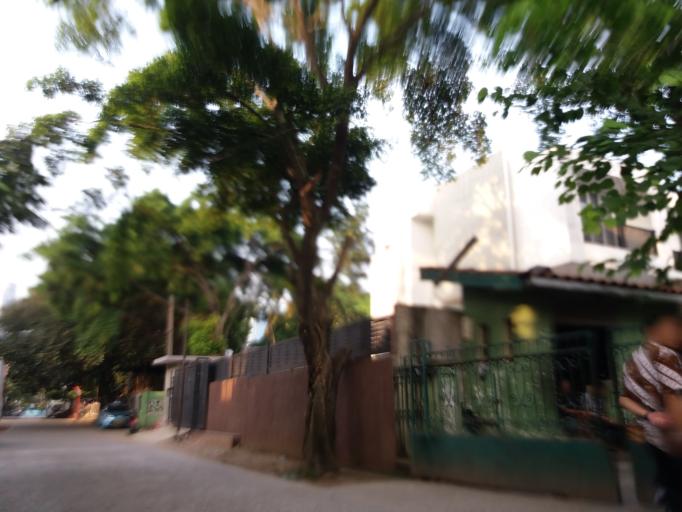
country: ID
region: Jakarta Raya
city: Jakarta
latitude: -6.2412
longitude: 106.8156
